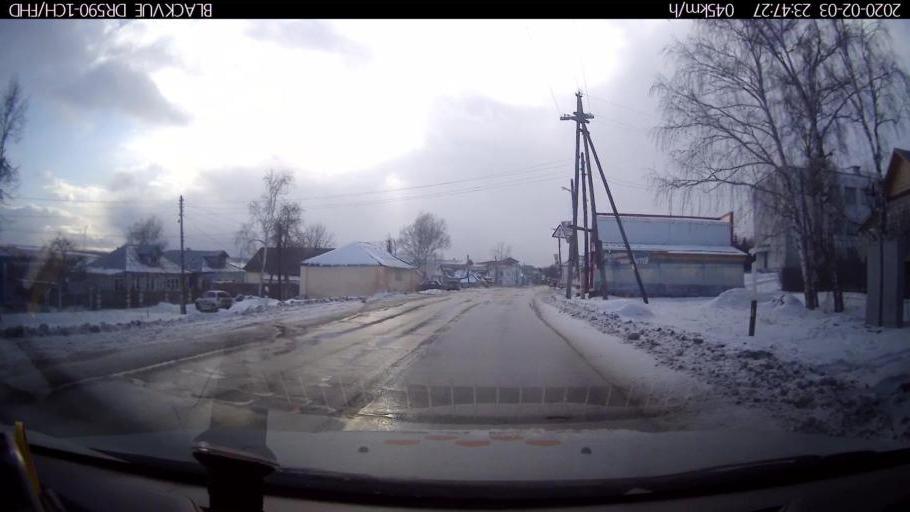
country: RU
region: Nizjnij Novgorod
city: Dal'neye Konstantinovo
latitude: 55.8108
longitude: 44.0988
